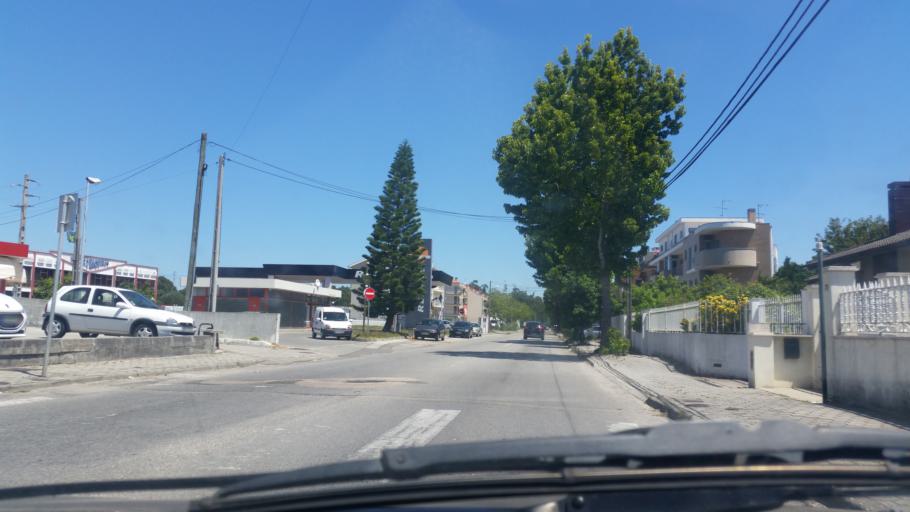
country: PT
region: Aveiro
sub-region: Aveiro
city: Aveiro
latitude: 40.6400
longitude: -8.6101
